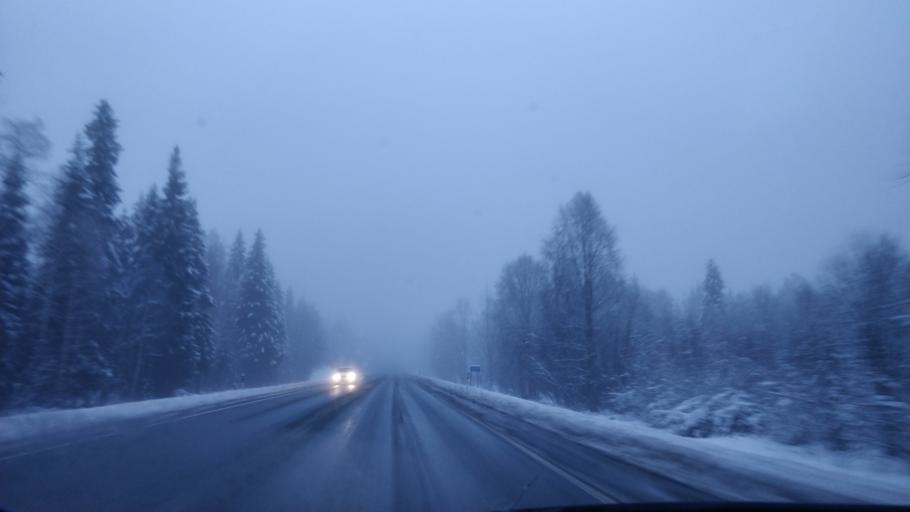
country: FI
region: Lapland
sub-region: Kemi-Tornio
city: Tervola
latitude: 66.1301
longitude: 24.8914
